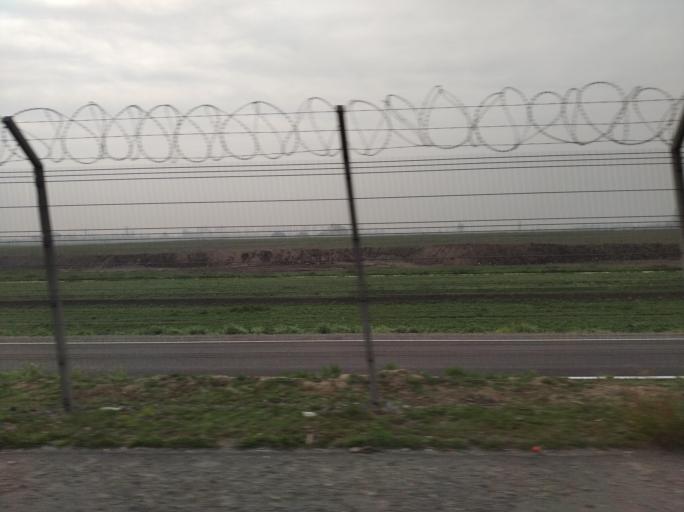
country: CL
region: Santiago Metropolitan
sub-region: Provincia de Chacabuco
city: Lampa
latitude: -33.3698
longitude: -70.8055
